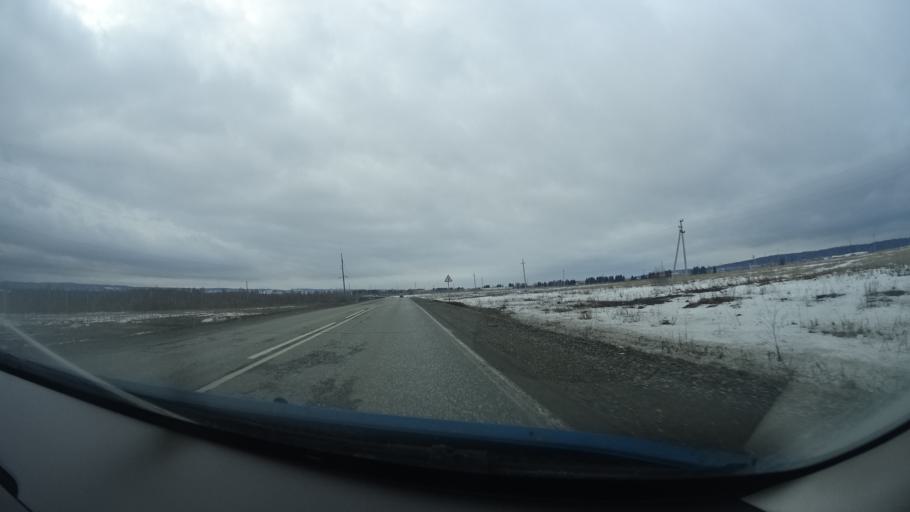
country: RU
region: Perm
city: Barda
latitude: 56.9557
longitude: 55.5813
